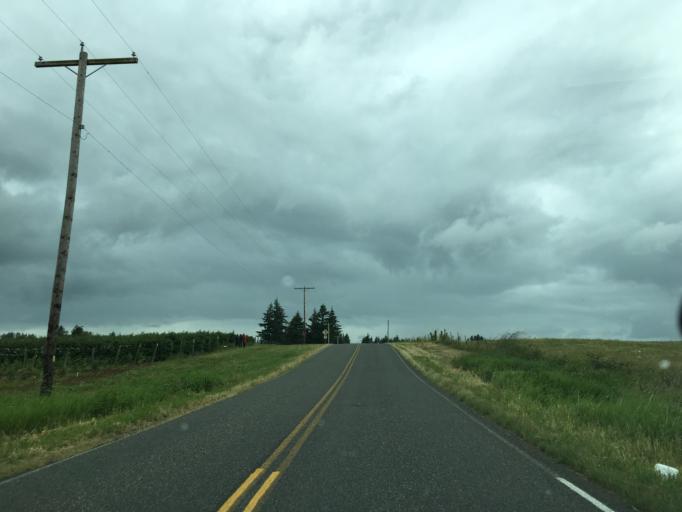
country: US
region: Washington
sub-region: Whatcom County
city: Everson
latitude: 48.9785
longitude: -122.3858
